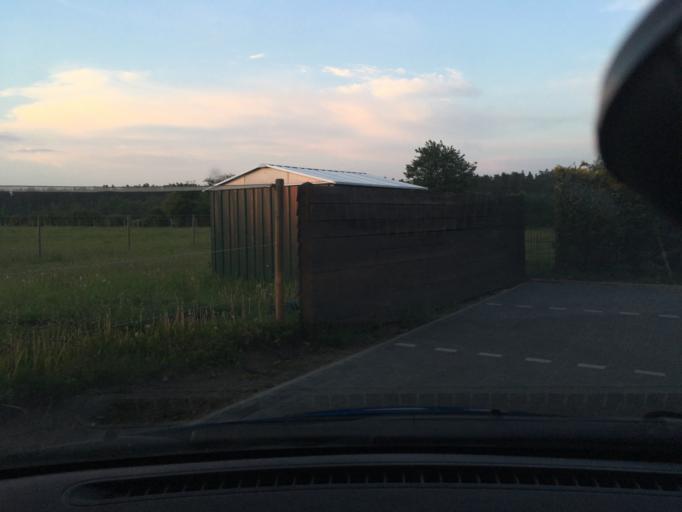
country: DE
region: Lower Saxony
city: Vierhofen
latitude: 53.2786
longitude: 10.2188
